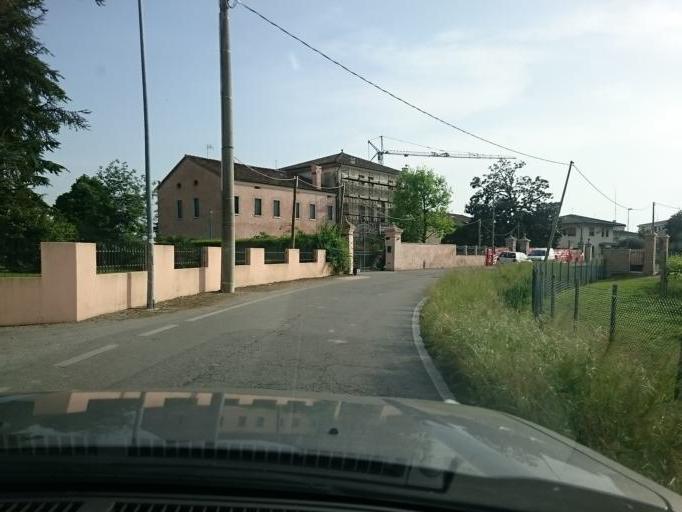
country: IT
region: Veneto
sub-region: Provincia di Venezia
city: Dolo
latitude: 45.4240
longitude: 12.0846
